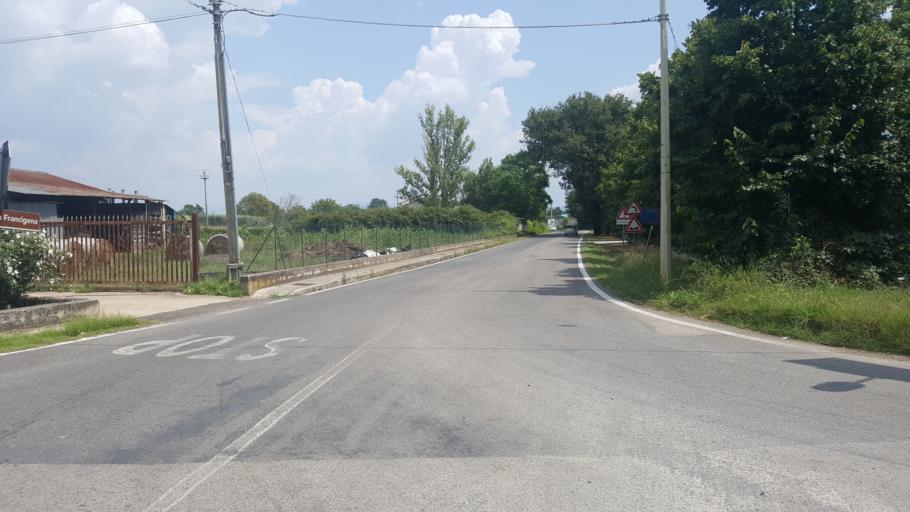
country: IT
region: Latium
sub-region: Provincia di Frosinone
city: Aquino
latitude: 41.5000
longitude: 13.6817
